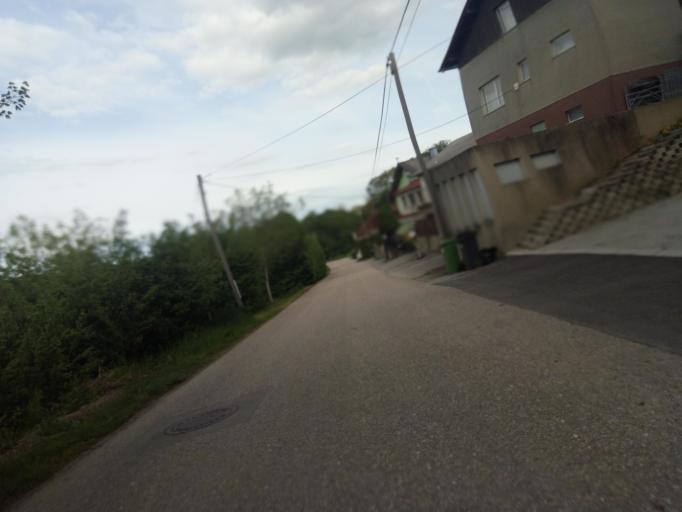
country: AT
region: Lower Austria
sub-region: Politischer Bezirk Modling
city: Breitenfurt bei Wien
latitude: 48.1336
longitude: 16.1463
